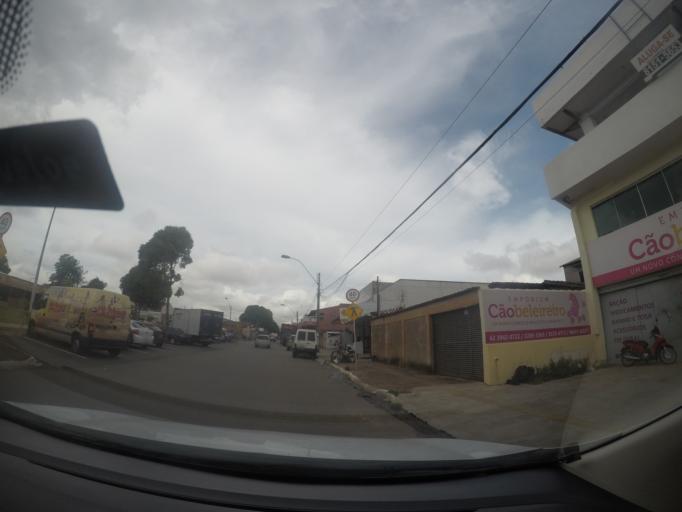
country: BR
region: Goias
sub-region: Goiania
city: Goiania
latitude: -16.7211
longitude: -49.3036
